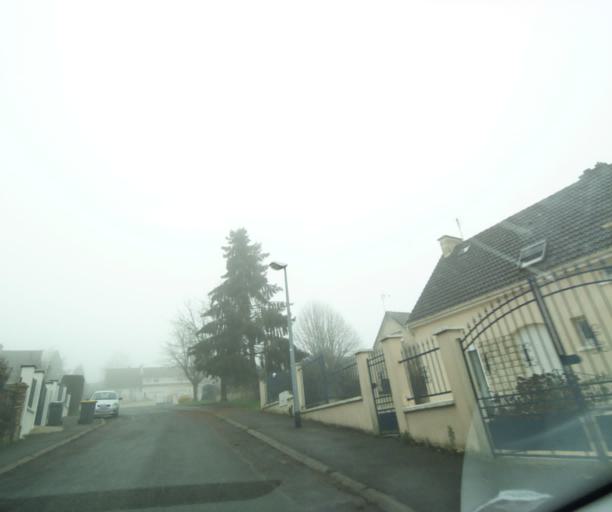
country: FR
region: Ile-de-France
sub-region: Departement de Seine-et-Marne
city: Longperrier
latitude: 49.0543
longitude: 2.6700
